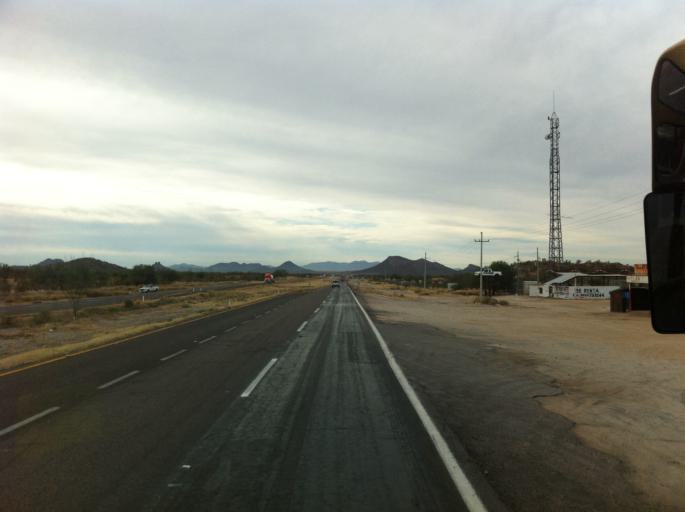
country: MX
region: Sonora
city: Hermosillo
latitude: 28.9608
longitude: -110.9633
